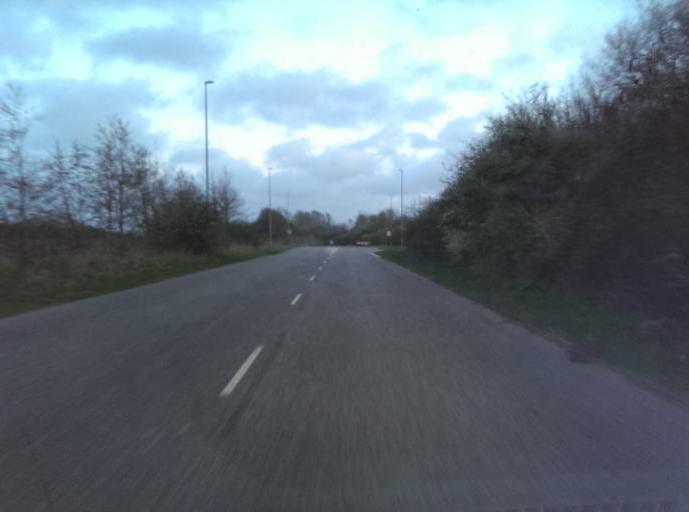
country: DK
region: South Denmark
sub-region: Esbjerg Kommune
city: Esbjerg
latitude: 55.4947
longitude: 8.5013
